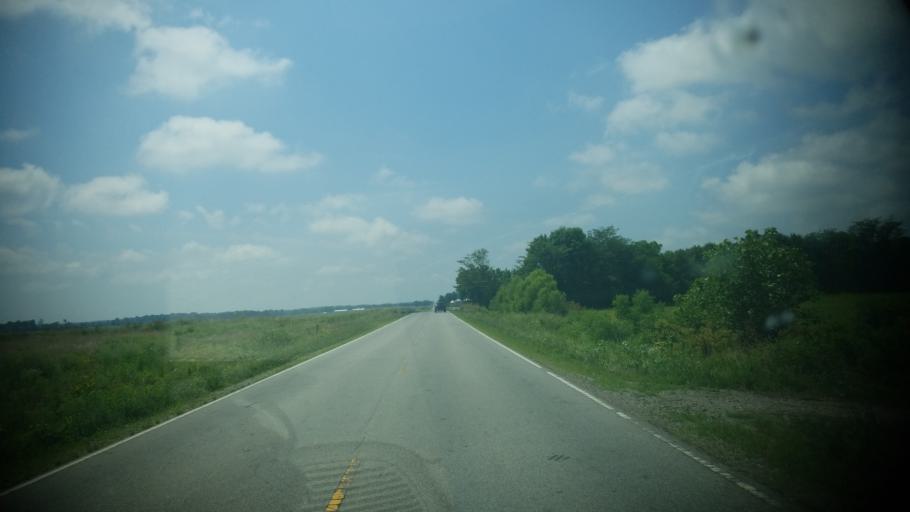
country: US
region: Illinois
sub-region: Wayne County
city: Fairfield
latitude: 38.4625
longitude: -88.3490
